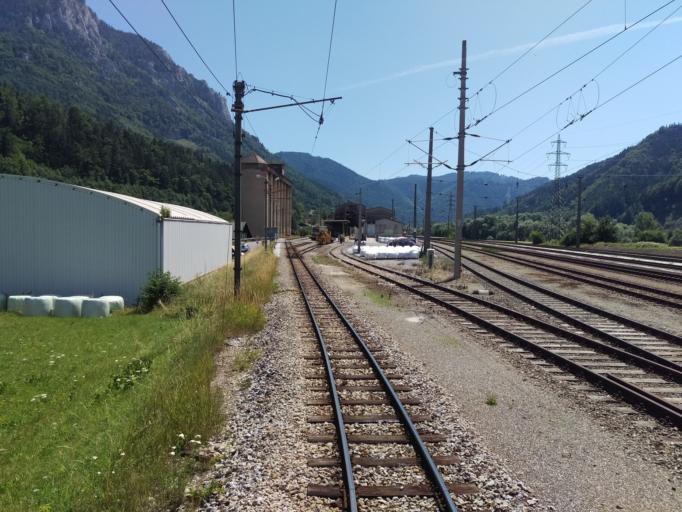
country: AT
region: Styria
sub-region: Politischer Bezirk Graz-Umgebung
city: Rothelstein
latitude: 47.3346
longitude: 15.3577
